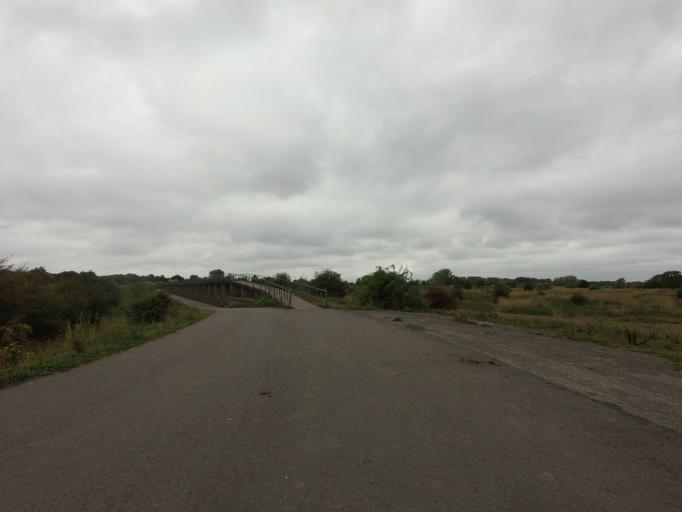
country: NL
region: Gelderland
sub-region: Gemeente Arnhem
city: Sterrenberg
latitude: 51.9722
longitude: 5.8713
